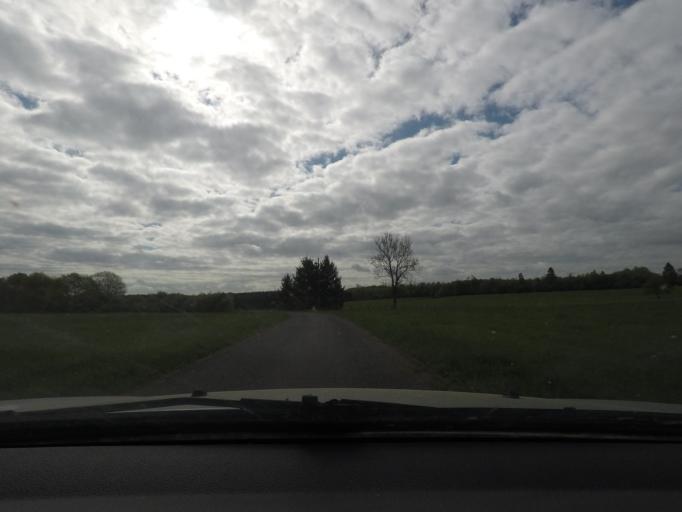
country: BE
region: Wallonia
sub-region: Province du Luxembourg
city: Habay-la-Vieille
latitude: 49.7090
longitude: 5.6001
